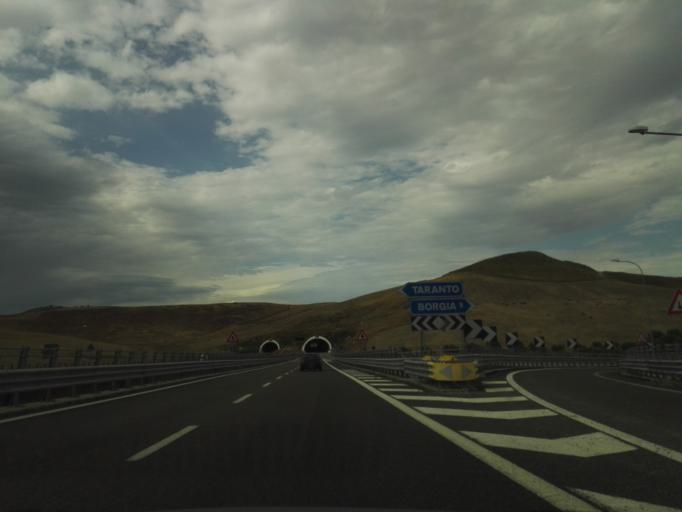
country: IT
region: Calabria
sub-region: Provincia di Catanzaro
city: Roccelletta
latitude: 38.8222
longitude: 16.5626
